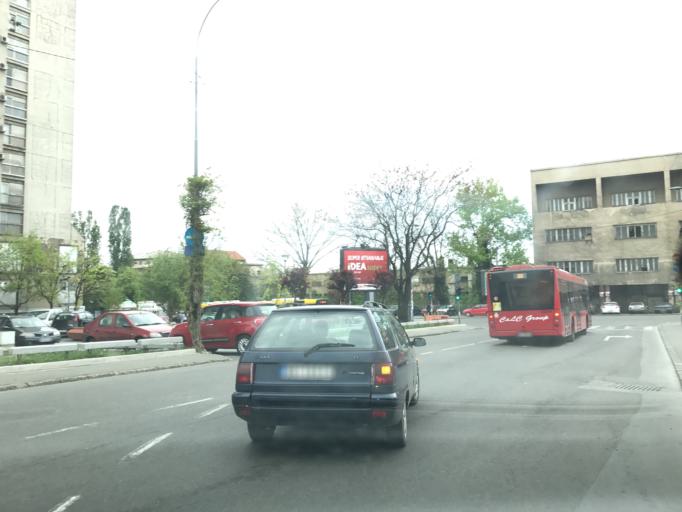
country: RS
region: Central Serbia
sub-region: Belgrade
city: Stari Grad
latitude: 44.8172
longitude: 20.4856
